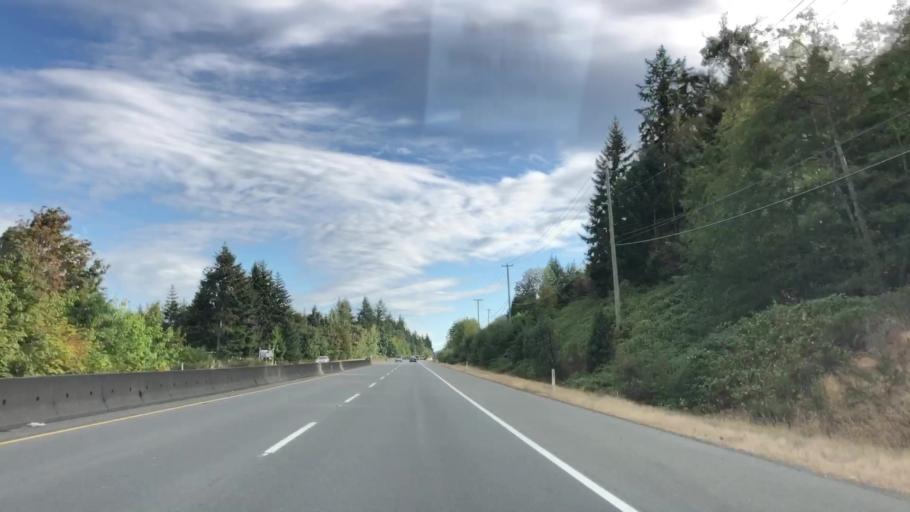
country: CA
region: British Columbia
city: North Saanich
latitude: 48.6348
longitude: -123.5500
